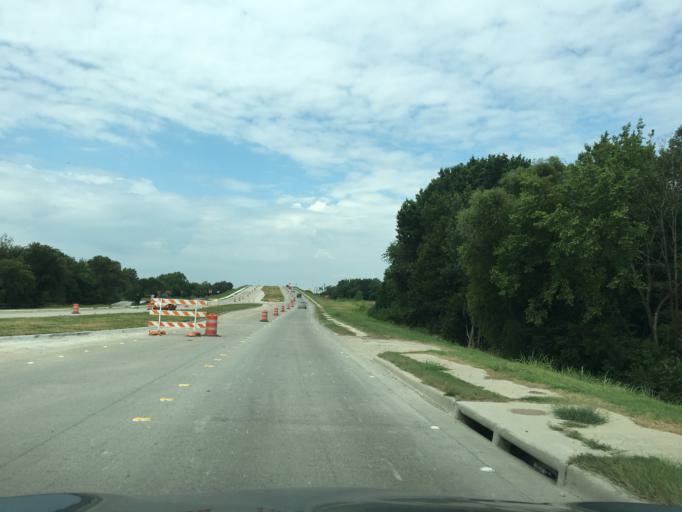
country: US
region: Texas
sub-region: Collin County
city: Melissa
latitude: 33.2775
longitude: -96.5714
